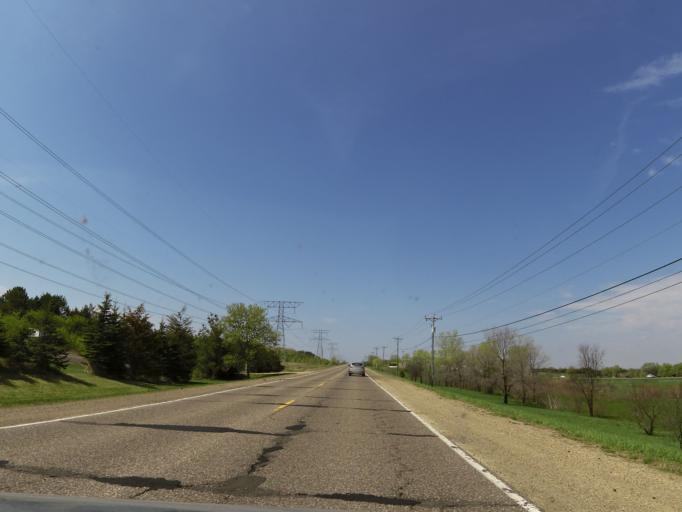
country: US
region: Minnesota
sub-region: Washington County
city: Lakeland
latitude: 44.9469
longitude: -92.8254
